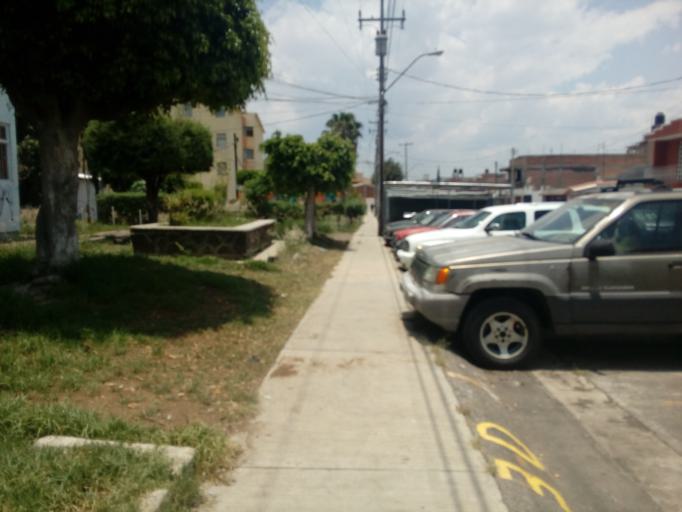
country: MX
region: Michoacan
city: Morelia
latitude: 19.7110
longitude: -101.2312
